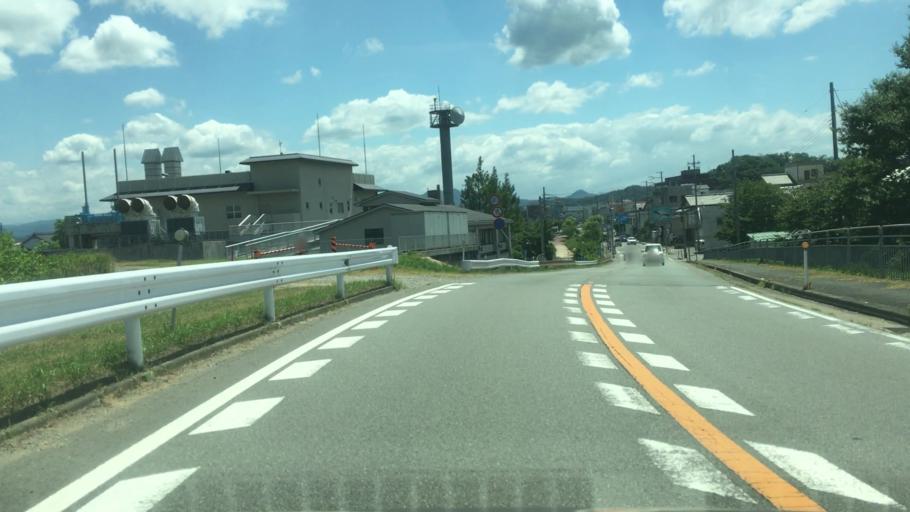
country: JP
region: Hyogo
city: Toyooka
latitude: 35.5474
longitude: 134.8263
